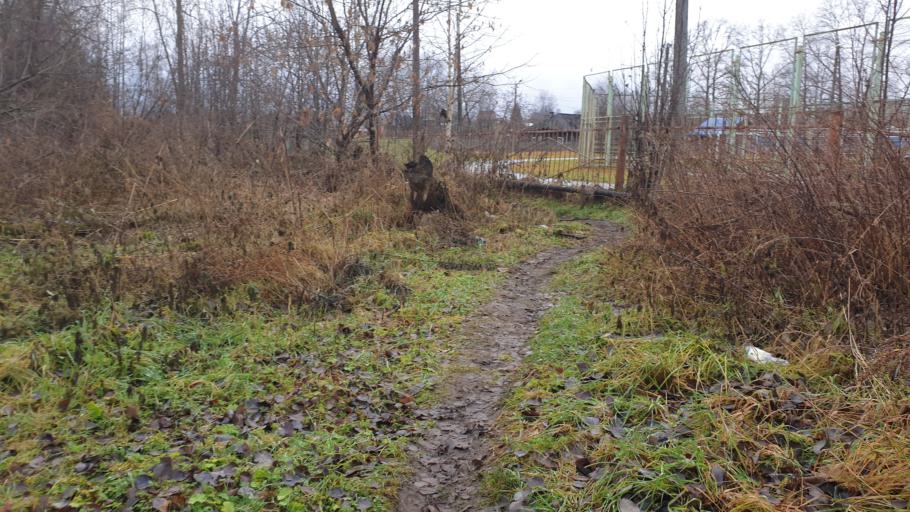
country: RU
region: Kirov
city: Kirs
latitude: 59.3352
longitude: 52.2403
